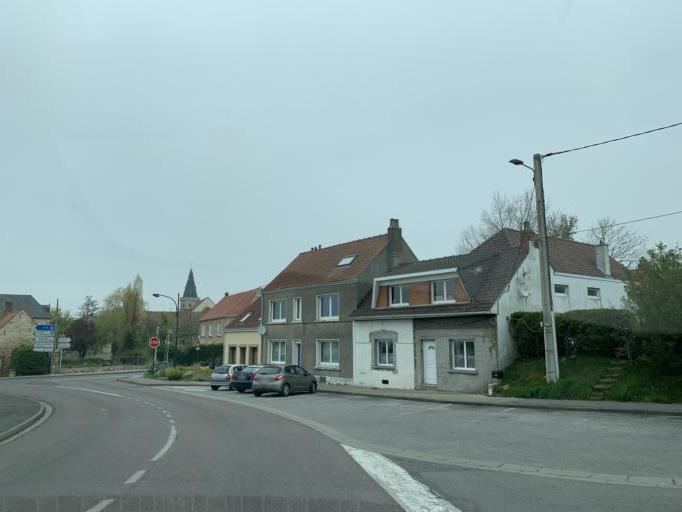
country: FR
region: Nord-Pas-de-Calais
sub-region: Departement du Pas-de-Calais
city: Marquise
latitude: 50.8104
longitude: 1.7080
